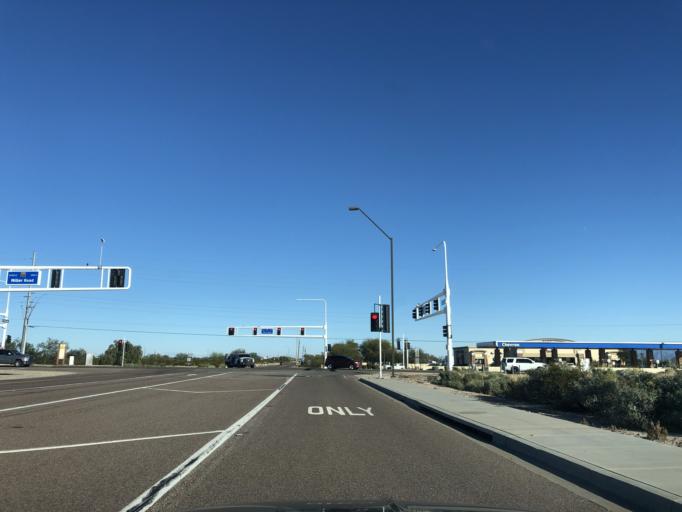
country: US
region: Arizona
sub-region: Maricopa County
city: Buckeye
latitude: 33.4280
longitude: -112.5917
